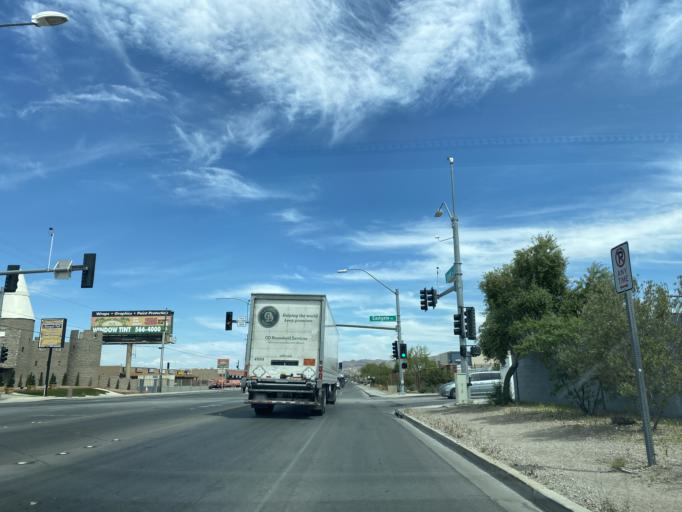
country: US
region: Nevada
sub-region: Clark County
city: Henderson
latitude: 36.0638
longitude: -115.0208
